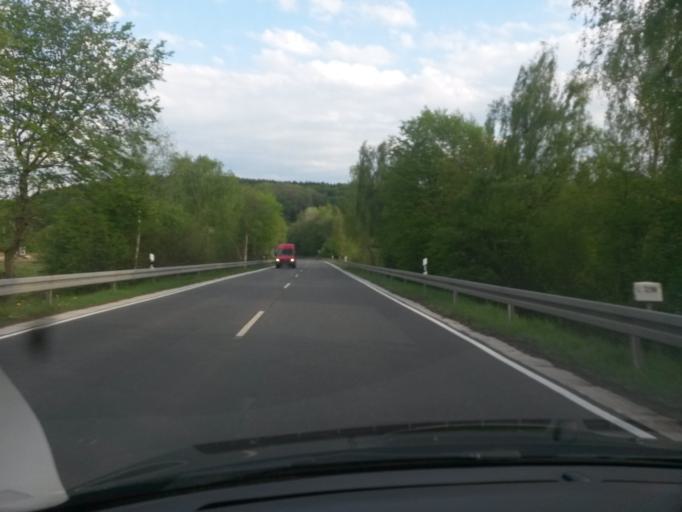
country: DE
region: Hesse
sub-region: Regierungsbezirk Kassel
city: Baunatal
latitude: 51.3120
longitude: 9.3760
